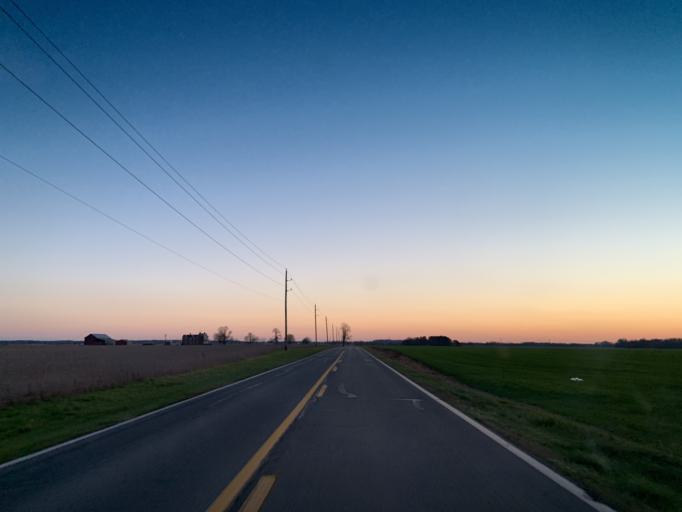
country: US
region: Delaware
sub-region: New Castle County
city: Middletown
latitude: 39.4193
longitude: -75.7430
